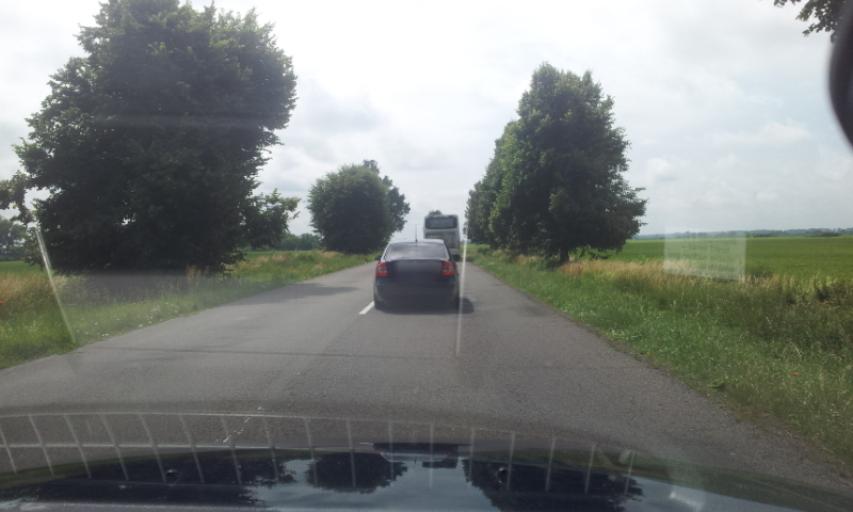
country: SK
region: Kosicky
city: Michalovce
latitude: 48.7266
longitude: 21.9575
